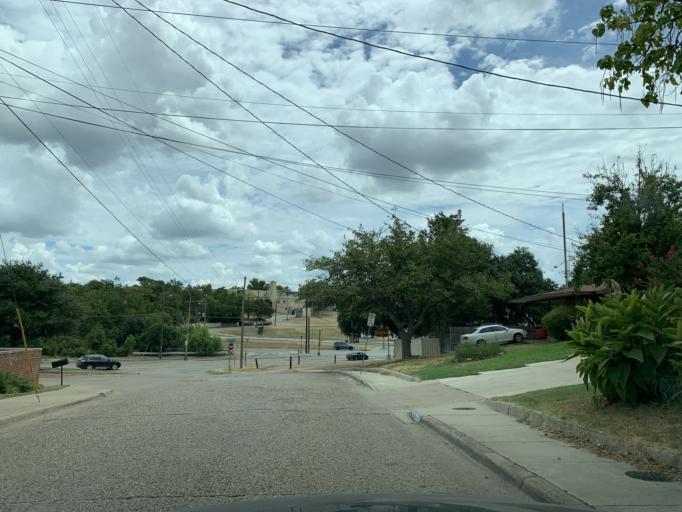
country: US
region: Texas
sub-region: Dallas County
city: Cockrell Hill
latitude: 32.7443
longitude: -96.8749
